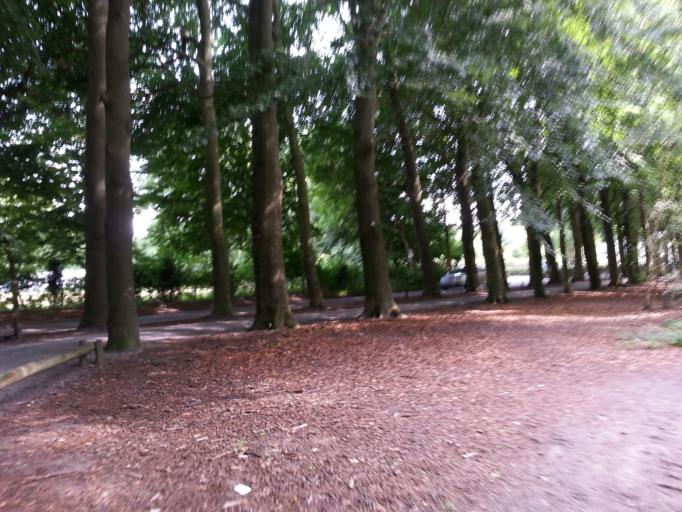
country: NL
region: Utrecht
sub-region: Gemeente Utrechtse Heuvelrug
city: Maarn
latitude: 52.0810
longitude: 5.3817
